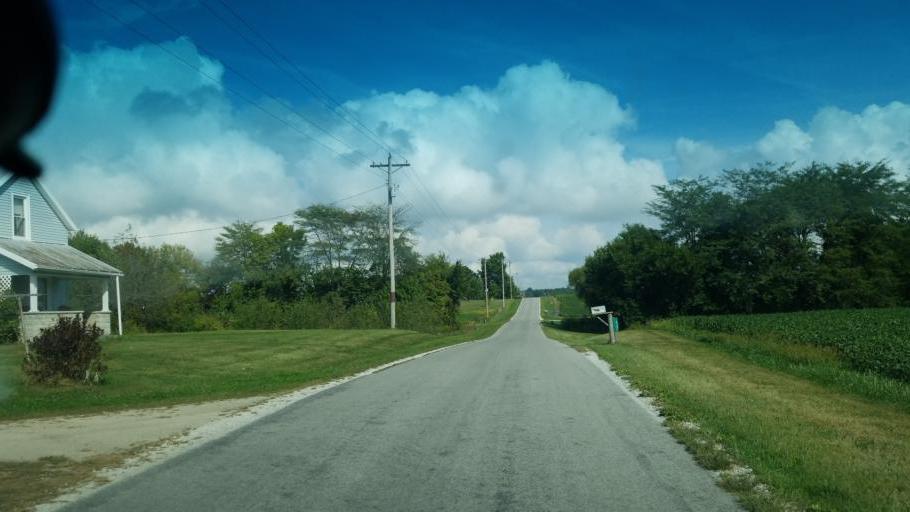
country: US
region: Ohio
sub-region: Wyandot County
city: Carey
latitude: 40.8988
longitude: -83.3992
